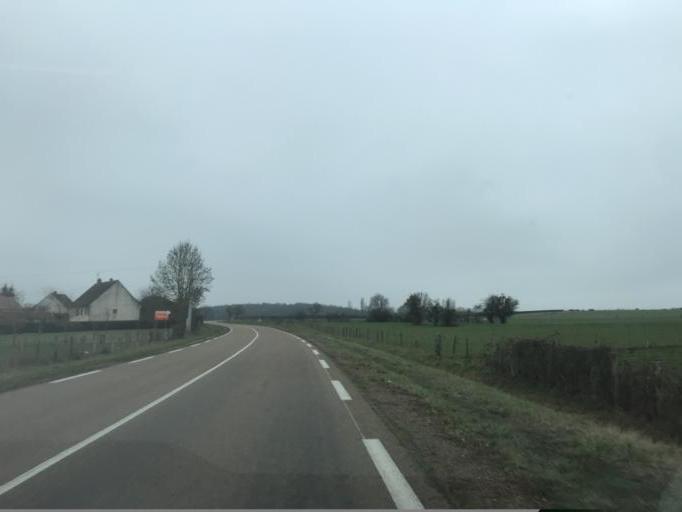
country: FR
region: Bourgogne
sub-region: Departement de l'Yonne
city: Avallon
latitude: 47.5011
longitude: 3.9792
